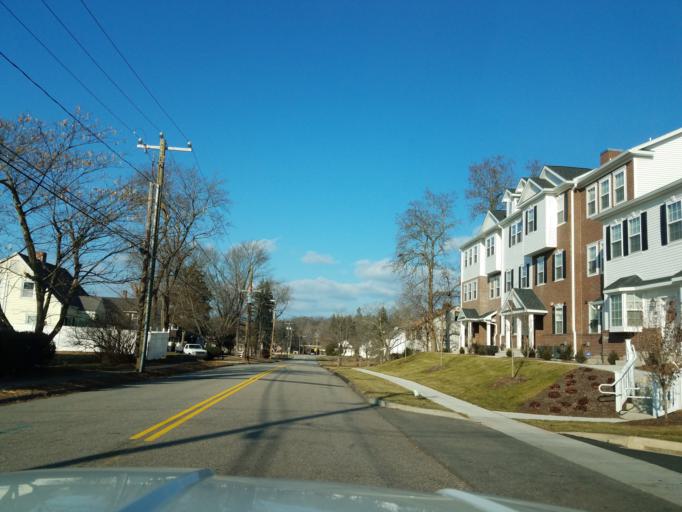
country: US
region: Connecticut
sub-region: Hartford County
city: Glastonbury
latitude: 41.7147
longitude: -72.6015
